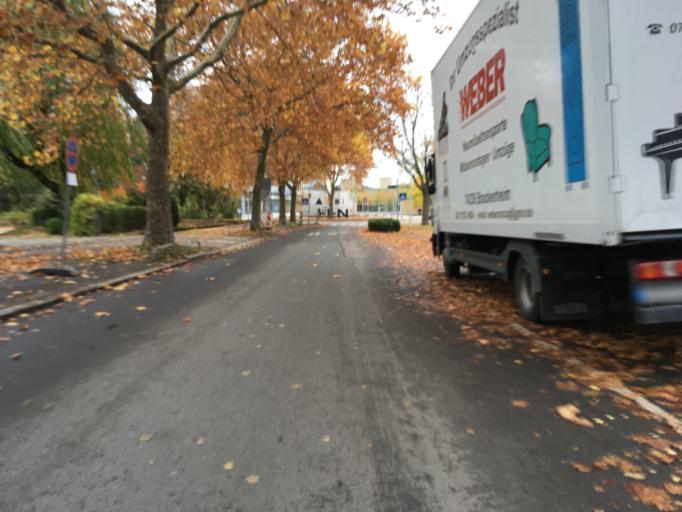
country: DE
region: Baden-Wuerttemberg
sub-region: Regierungsbezirk Stuttgart
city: Flein
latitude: 49.1207
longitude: 9.2115
